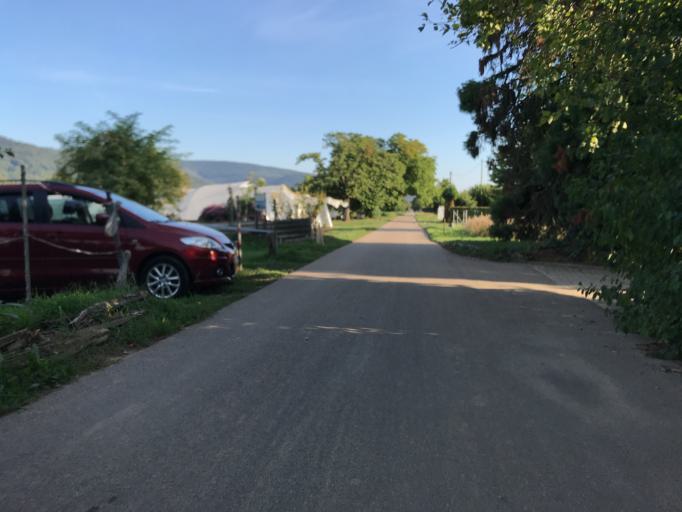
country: DE
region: Baden-Wuerttemberg
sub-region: Karlsruhe Region
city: Dossenheim
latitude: 49.4379
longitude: 8.6661
